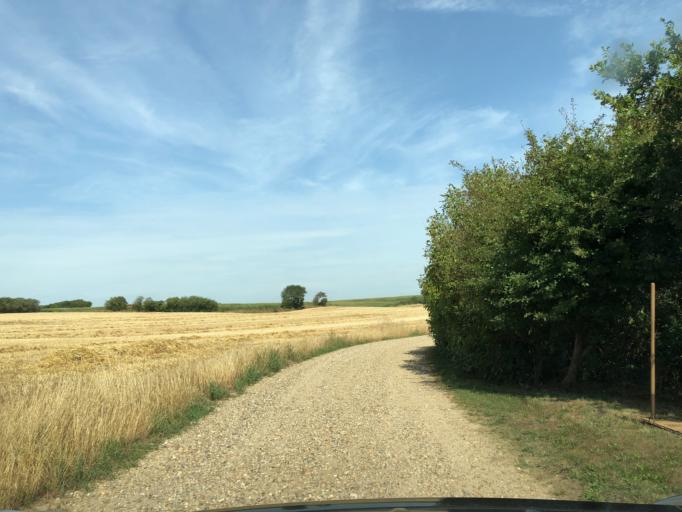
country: DK
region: Central Jutland
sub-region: Ringkobing-Skjern Kommune
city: Skjern
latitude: 55.9964
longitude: 8.4969
